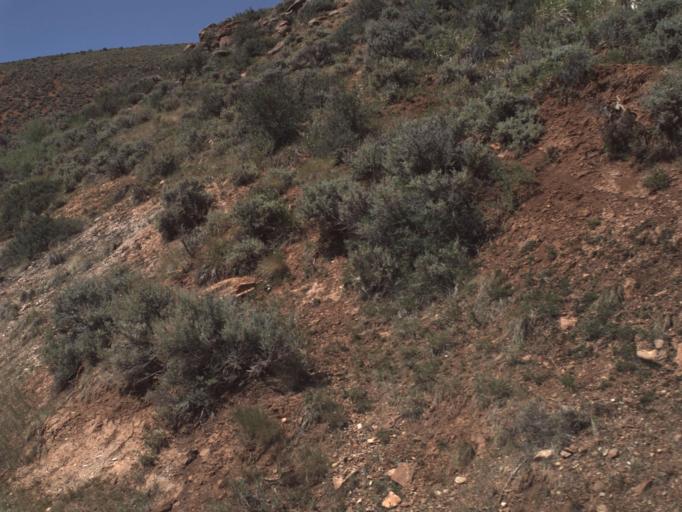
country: US
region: Utah
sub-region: Rich County
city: Randolph
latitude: 41.4793
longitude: -111.3678
